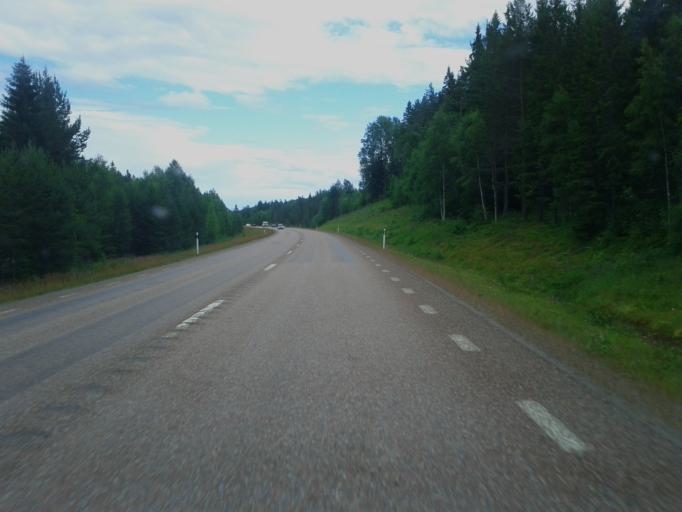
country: SE
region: Dalarna
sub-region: Faluns Kommun
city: Bjursas
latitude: 60.7506
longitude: 15.3524
